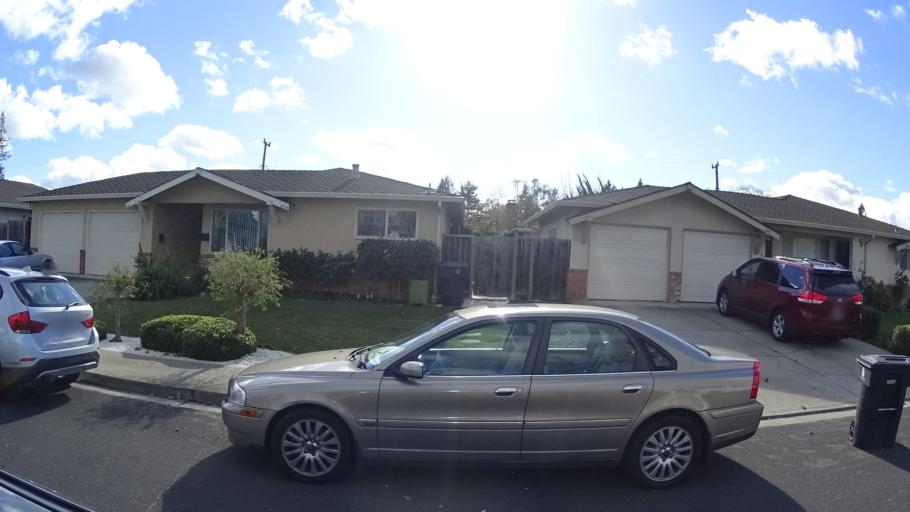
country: US
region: California
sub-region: Santa Clara County
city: Mountain View
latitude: 37.3817
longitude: -122.0600
